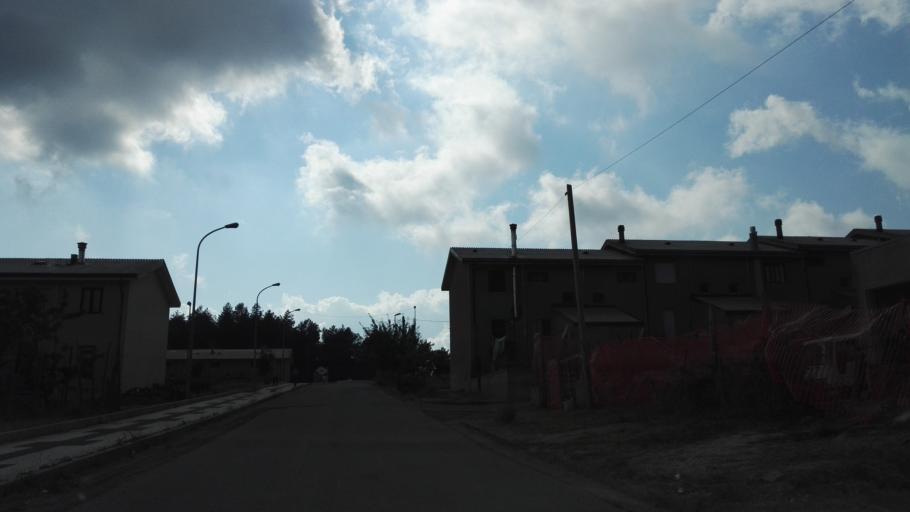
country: IT
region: Calabria
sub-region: Provincia di Vibo-Valentia
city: Nardodipace
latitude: 38.4774
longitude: 16.3407
